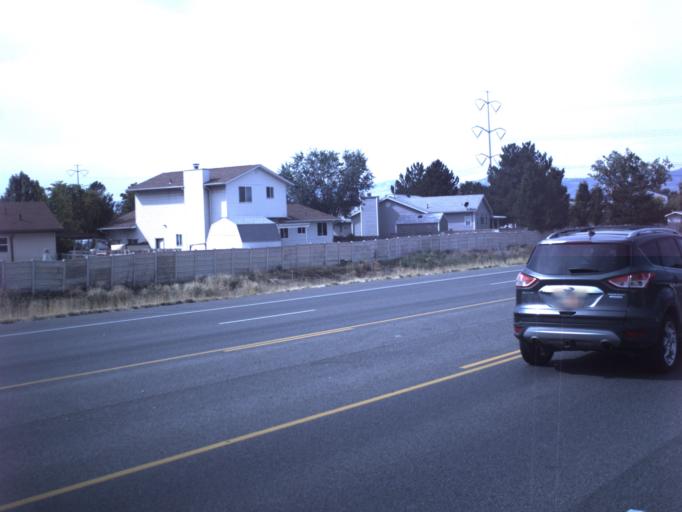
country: US
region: Utah
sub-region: Salt Lake County
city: Taylorsville
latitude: 40.6531
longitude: -111.9158
